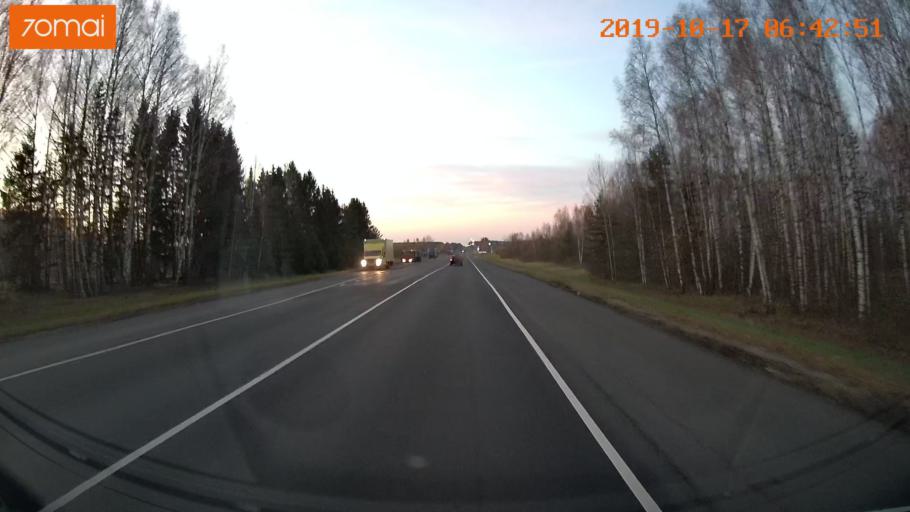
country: RU
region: Vladimir
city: Kideksha
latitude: 56.5955
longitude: 40.5556
